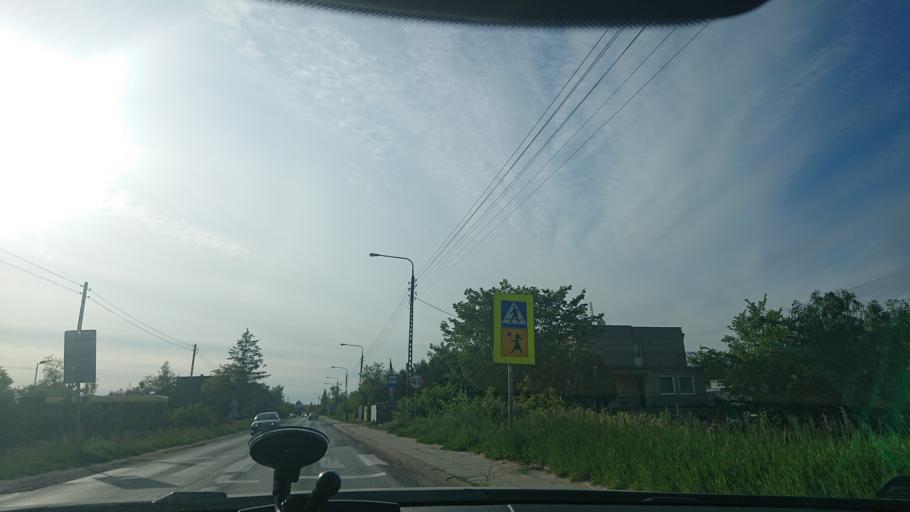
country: PL
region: Greater Poland Voivodeship
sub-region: Powiat gnieznienski
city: Gniezno
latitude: 52.5420
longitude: 17.5774
